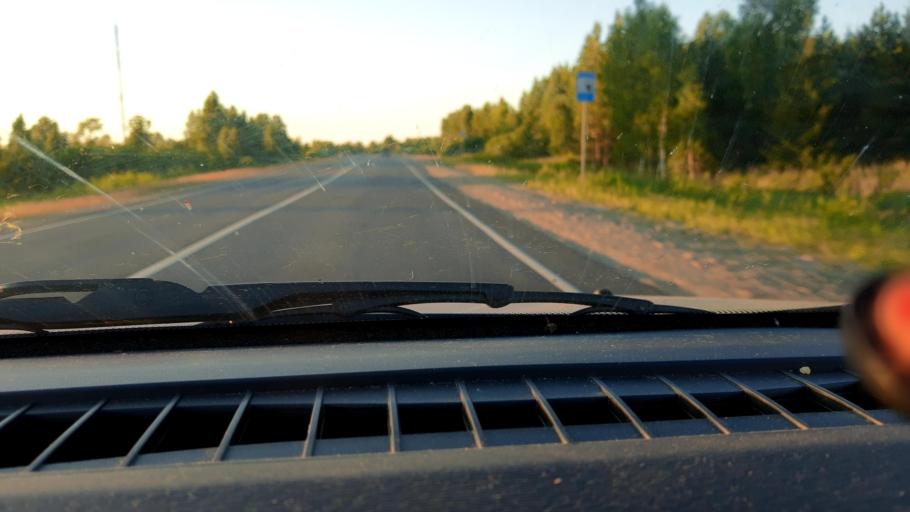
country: RU
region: Nizjnij Novgorod
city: Krasnyye Baki
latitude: 57.0819
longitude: 45.1458
